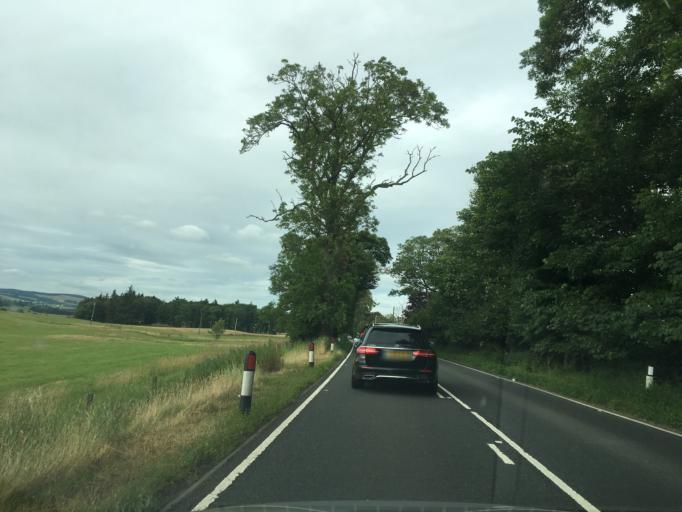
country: GB
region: Scotland
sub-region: South Lanarkshire
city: Biggar
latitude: 55.5660
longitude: -3.6023
